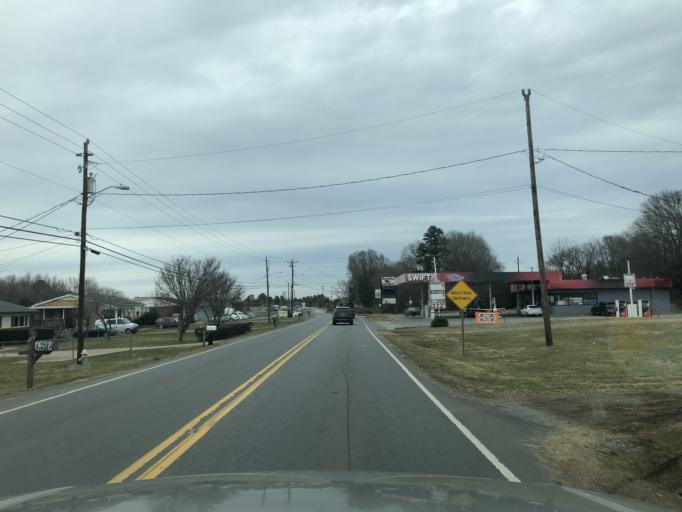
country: US
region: North Carolina
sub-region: Cleveland County
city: Shelby
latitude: 35.2952
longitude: -81.4878
